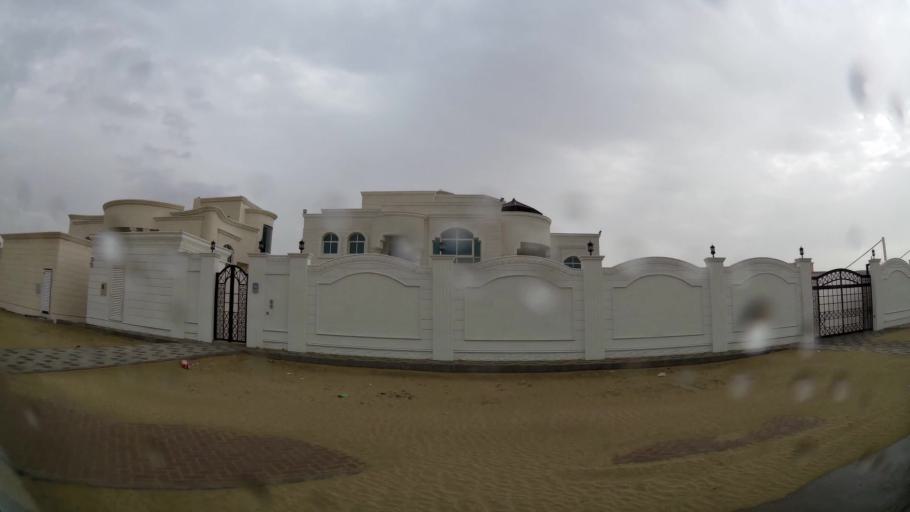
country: AE
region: Abu Dhabi
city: Abu Dhabi
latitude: 24.3709
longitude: 54.6305
